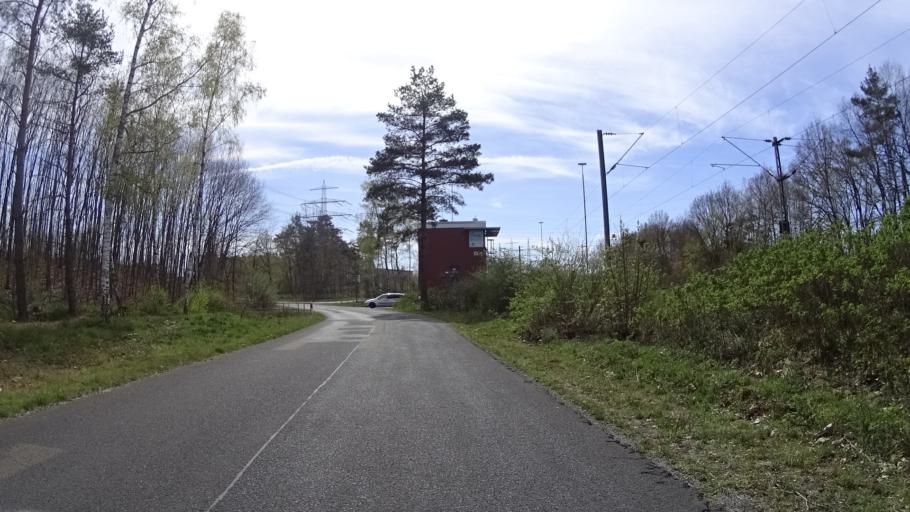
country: DE
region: Lower Saxony
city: Lingen
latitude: 52.4733
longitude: 7.3134
